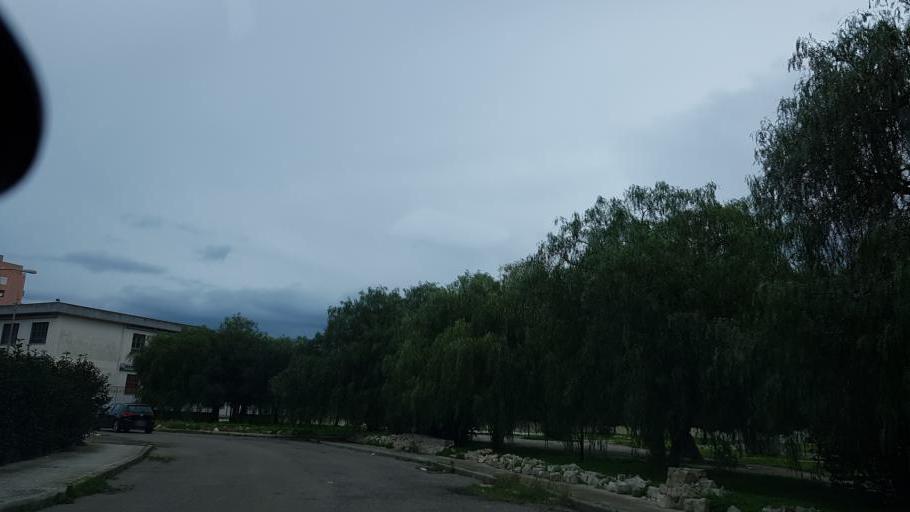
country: IT
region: Apulia
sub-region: Provincia di Brindisi
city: Brindisi
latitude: 40.6304
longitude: 17.9545
